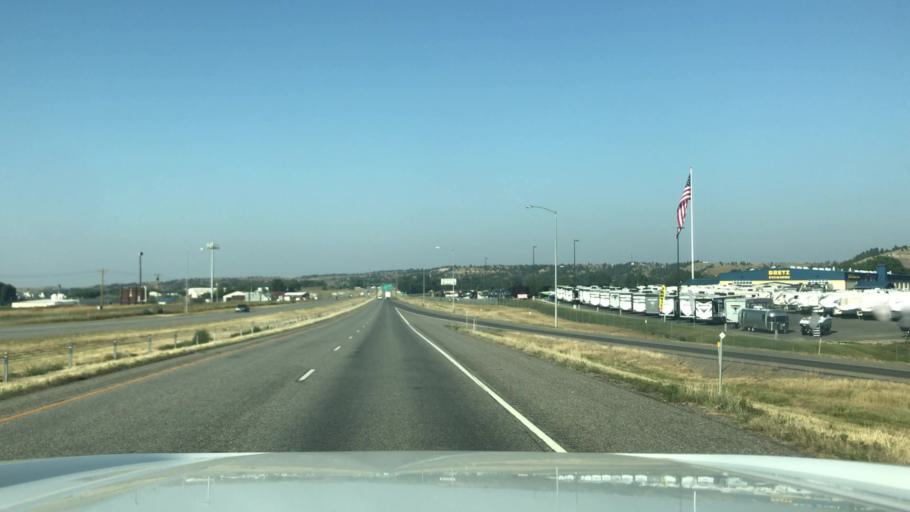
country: US
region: Montana
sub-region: Yellowstone County
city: Lockwood
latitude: 45.8163
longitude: -108.4118
